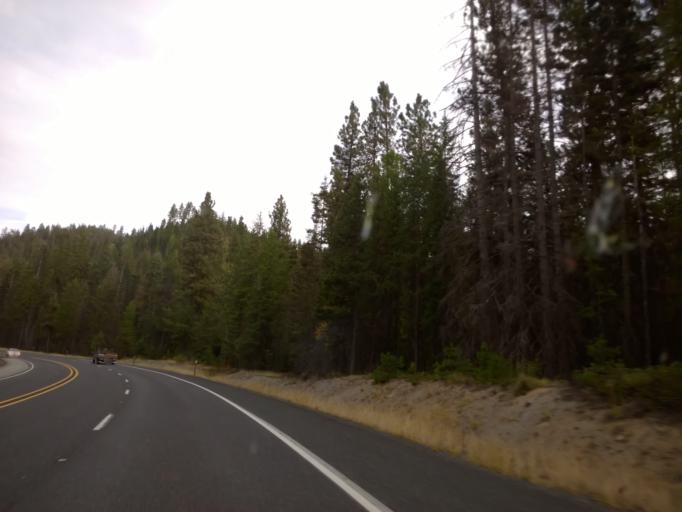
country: US
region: Washington
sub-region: Chelan County
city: Cashmere
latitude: 47.3635
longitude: -120.5768
